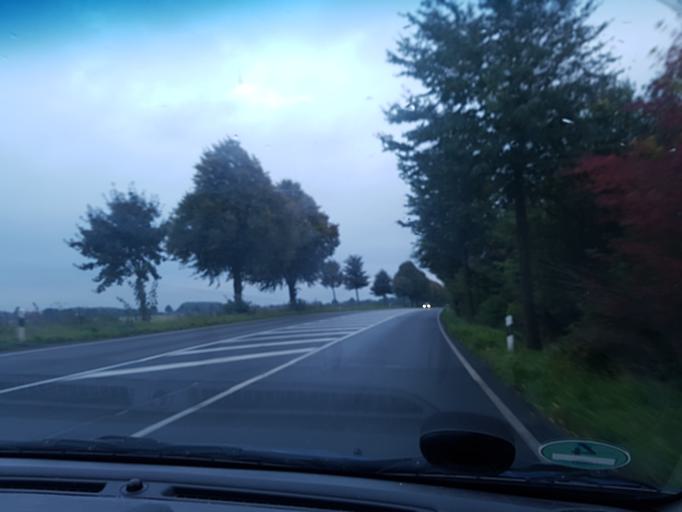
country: DE
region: Lower Saxony
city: Pattensen
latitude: 52.2852
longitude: 9.7562
